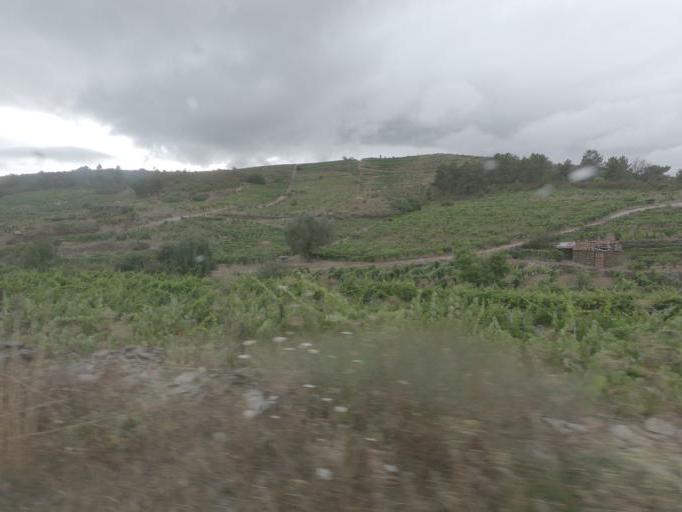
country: PT
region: Vila Real
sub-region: Sabrosa
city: Sabrosa
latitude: 41.2344
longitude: -7.4951
